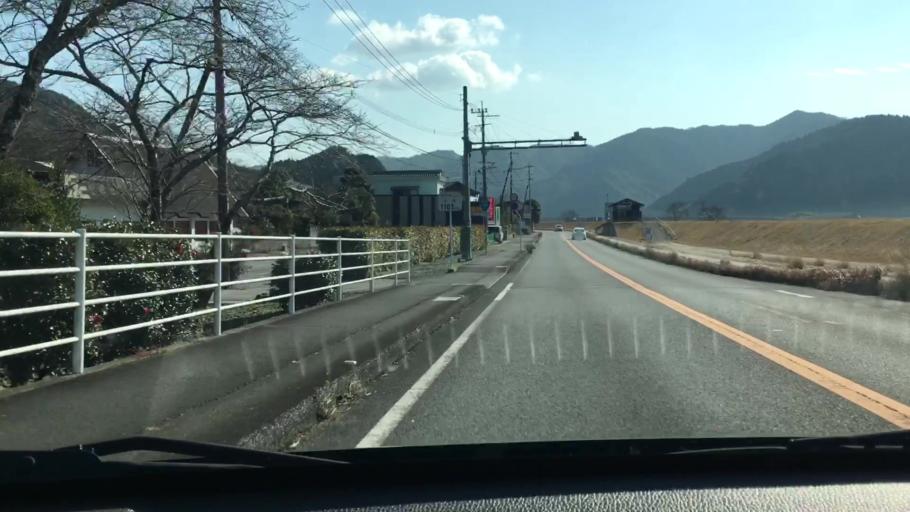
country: JP
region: Oita
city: Saiki
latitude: 32.9612
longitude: 131.8400
